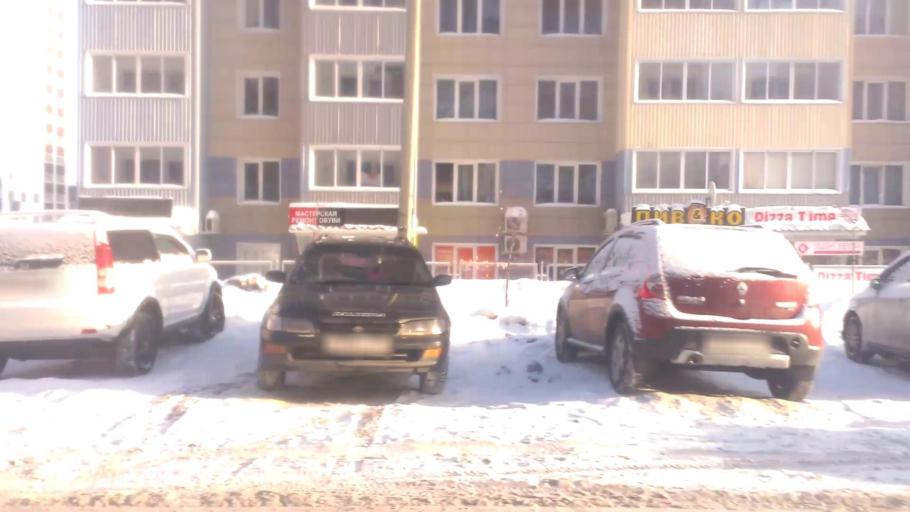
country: RU
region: Altai Krai
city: Novosilikatnyy
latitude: 53.3447
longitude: 83.6556
